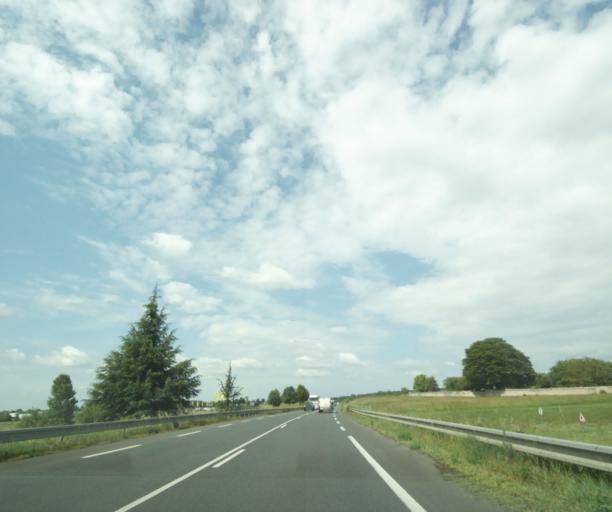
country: FR
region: Pays de la Loire
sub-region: Departement de Maine-et-Loire
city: Distre
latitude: 47.2237
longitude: -0.1168
